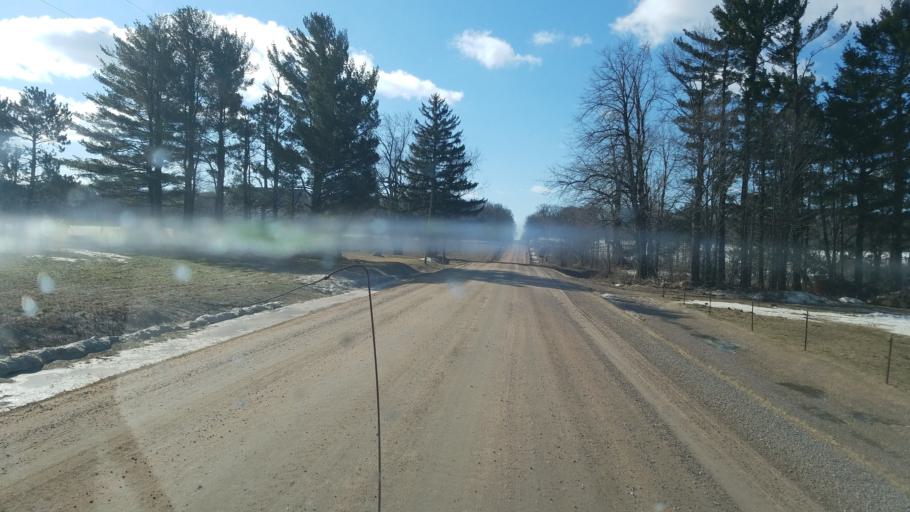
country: US
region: Wisconsin
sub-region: Clark County
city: Loyal
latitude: 44.6661
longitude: -90.4561
